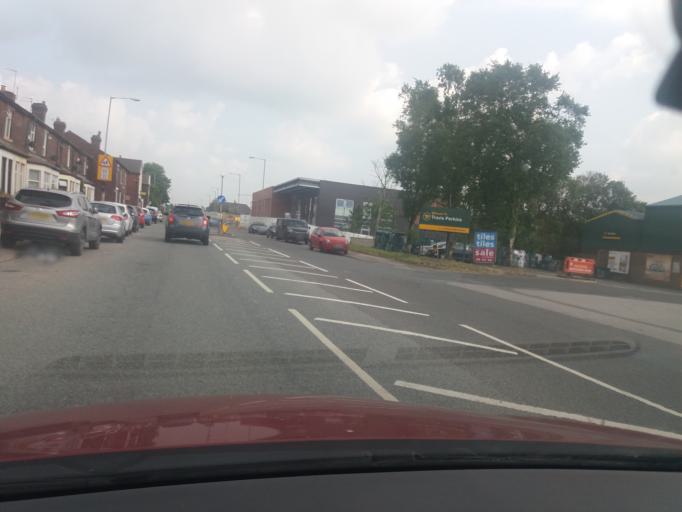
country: GB
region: England
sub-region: Borough of Bolton
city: Horwich
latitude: 53.5912
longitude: -2.5386
